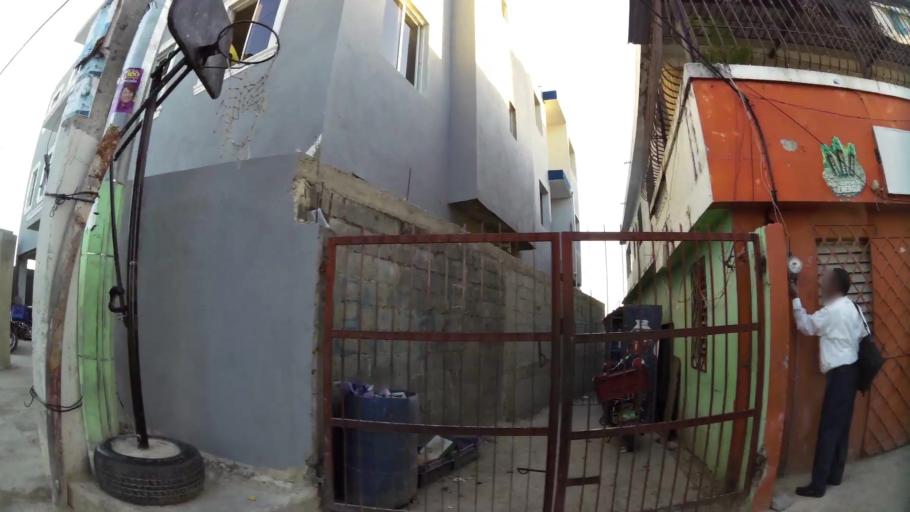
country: DO
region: Nacional
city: Santo Domingo
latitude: 18.4953
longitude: -69.9629
